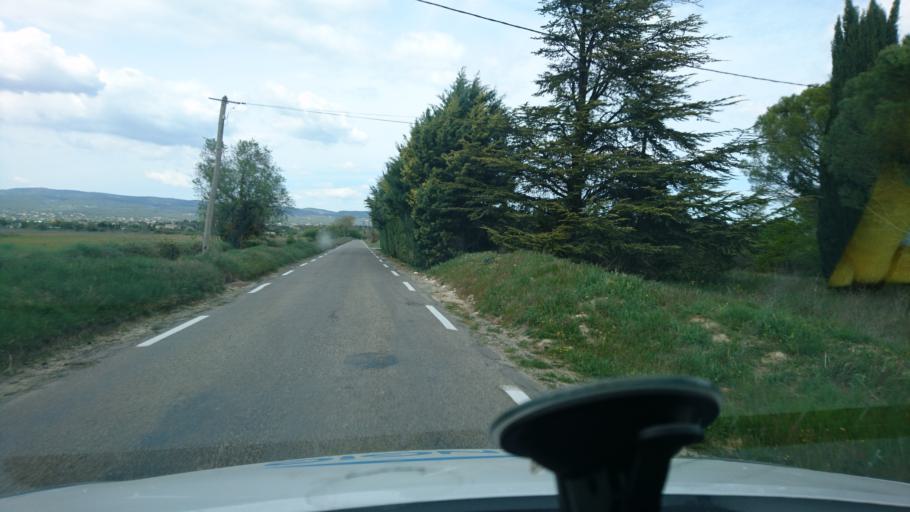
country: FR
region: Provence-Alpes-Cote d'Azur
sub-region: Departement du Vaucluse
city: Maubec
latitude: 43.8609
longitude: 5.1609
